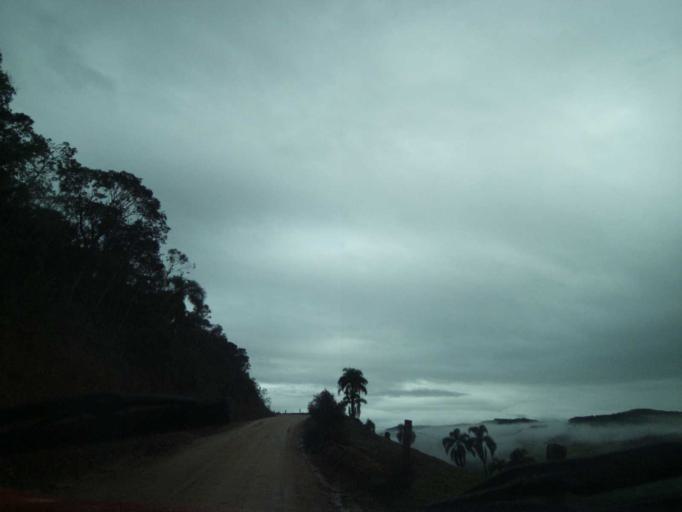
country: BR
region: Santa Catarina
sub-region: Anitapolis
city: Anitapolis
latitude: -27.9256
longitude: -49.1831
